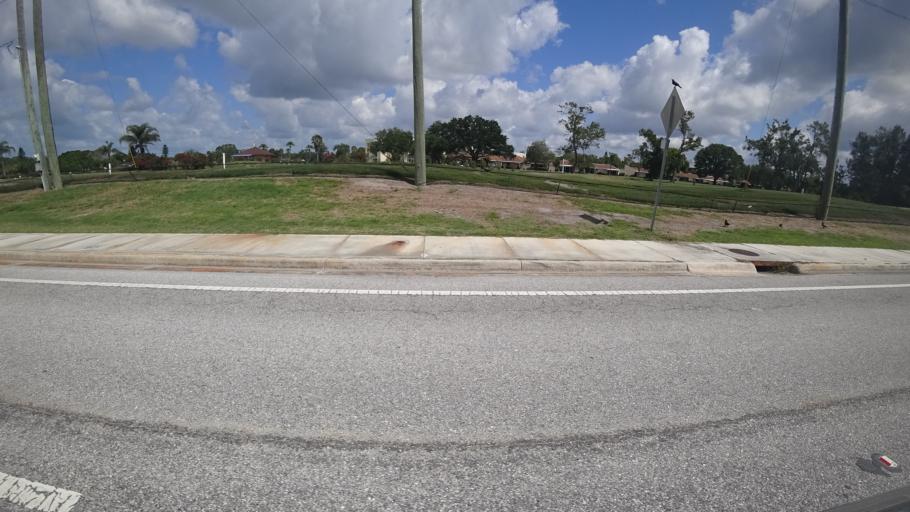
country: US
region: Florida
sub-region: Manatee County
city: Bayshore Gardens
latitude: 27.4292
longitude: -82.6030
